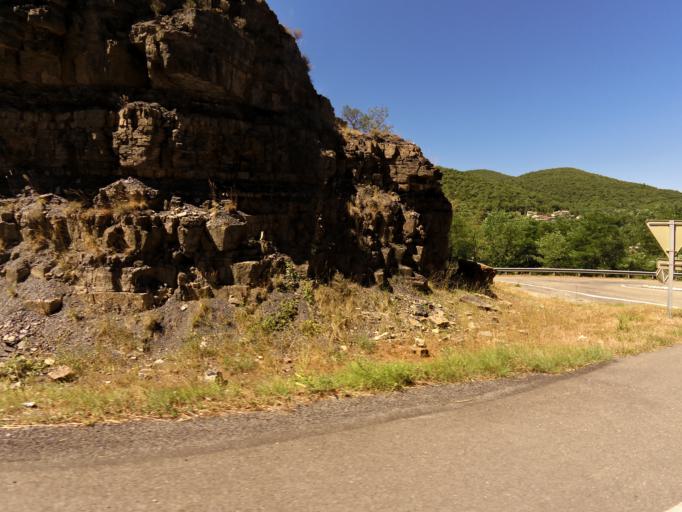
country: FR
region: Languedoc-Roussillon
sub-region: Departement du Gard
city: Saint-Jean-du-Gard
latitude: 44.0816
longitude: 3.9232
